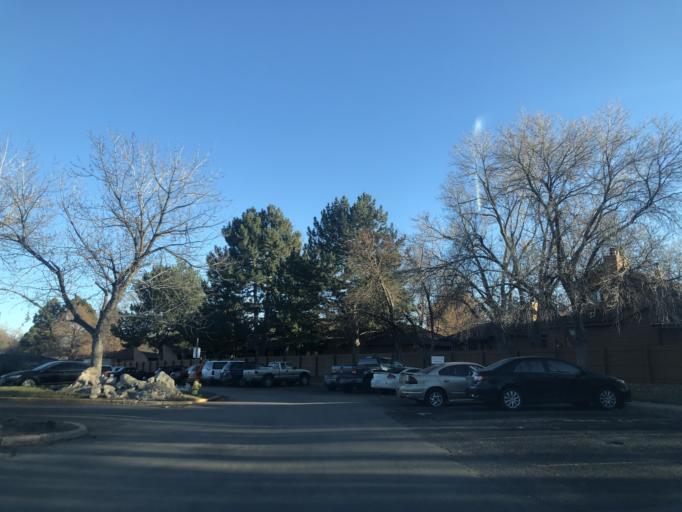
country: US
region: Colorado
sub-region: Adams County
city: Aurora
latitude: 39.7187
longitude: -104.8178
